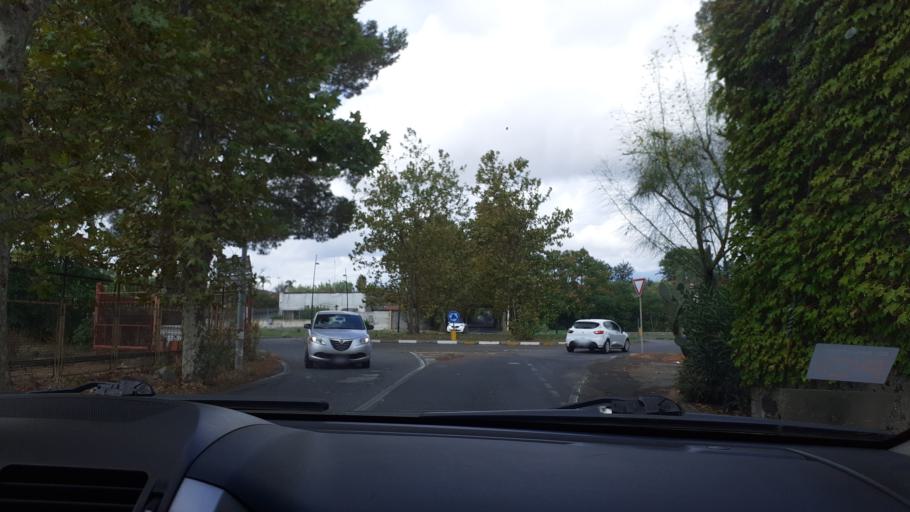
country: IT
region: Sicily
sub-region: Catania
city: San Giovanni la Punta
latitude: 37.5708
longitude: 15.1009
